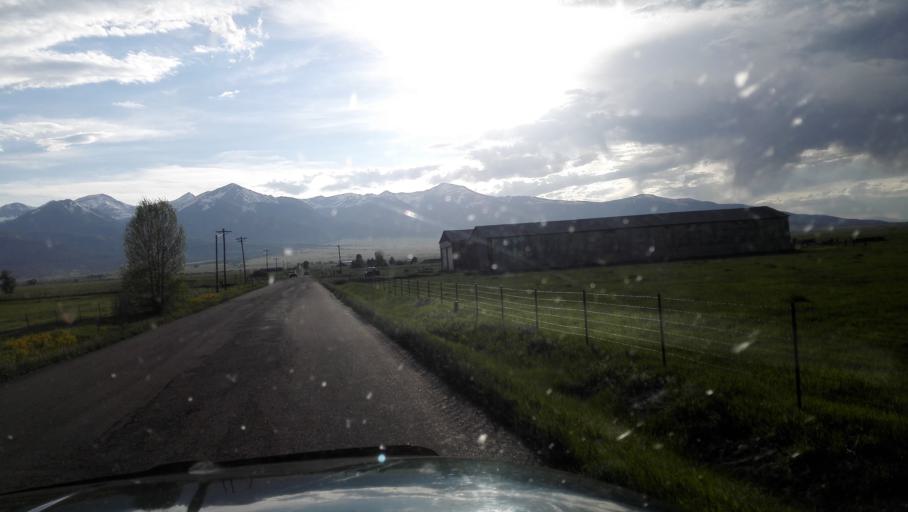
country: US
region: Colorado
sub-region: Custer County
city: Westcliffe
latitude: 38.1315
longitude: -105.4843
